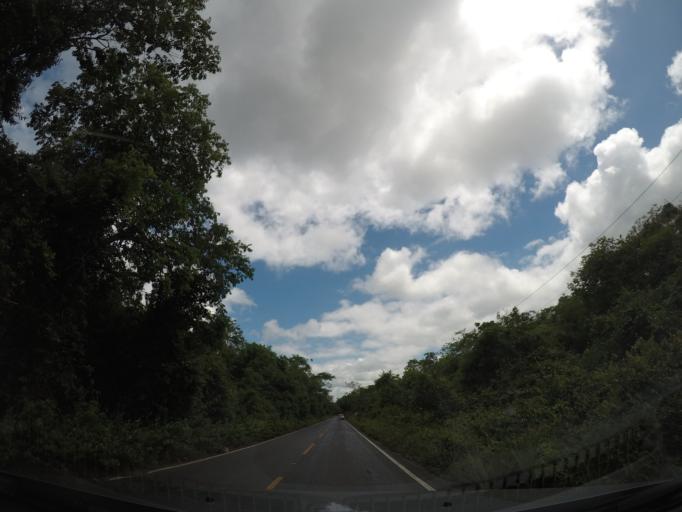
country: BR
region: Bahia
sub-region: Iraquara
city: Iraquara
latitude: -12.4925
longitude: -41.3627
